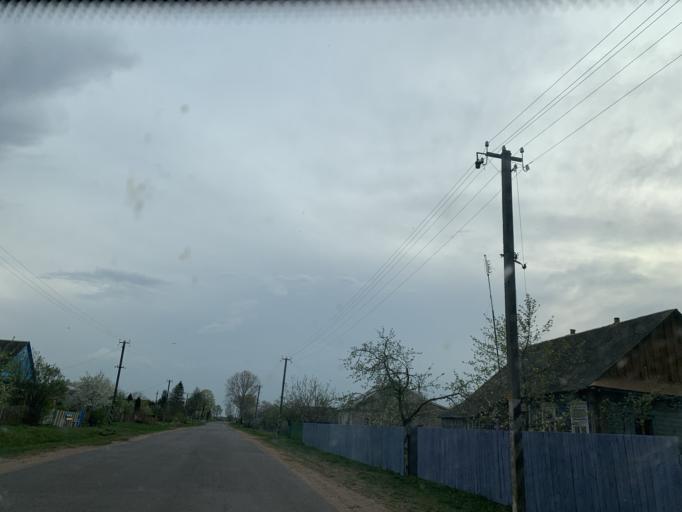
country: BY
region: Minsk
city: Kapyl'
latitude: 53.2764
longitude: 26.9710
